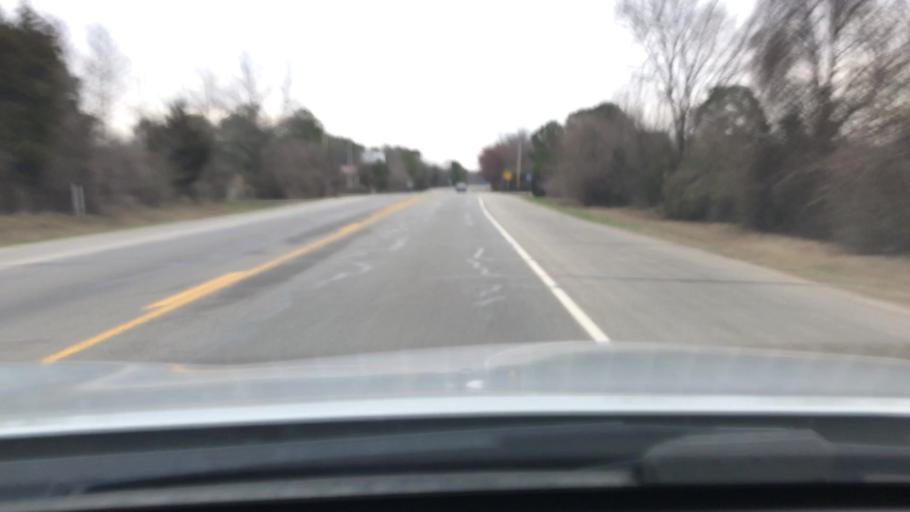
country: US
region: Arkansas
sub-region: Hempstead County
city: Hope
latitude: 33.6879
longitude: -93.5858
